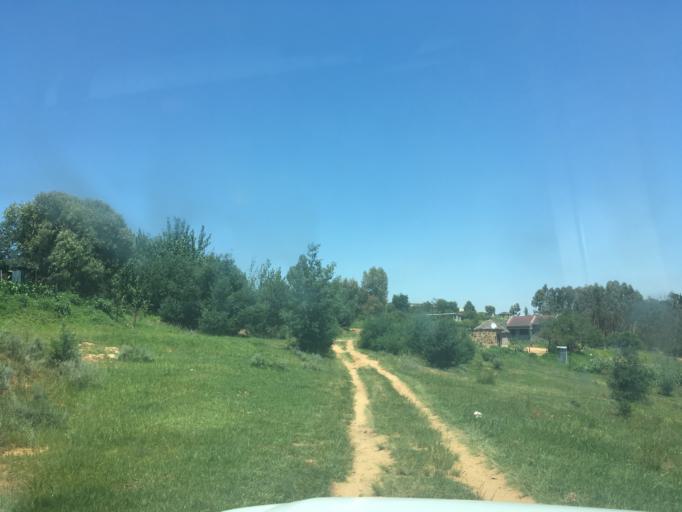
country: LS
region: Butha-Buthe
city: Butha-Buthe
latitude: -28.7261
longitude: 28.3646
